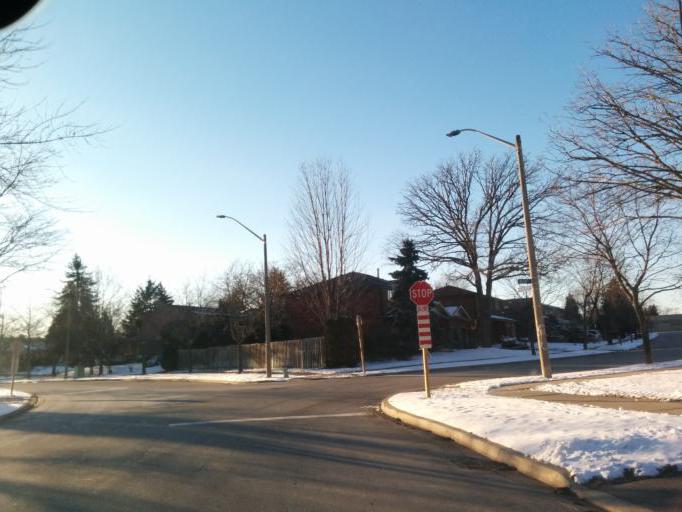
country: CA
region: Ontario
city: Mississauga
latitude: 43.5457
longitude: -79.6205
